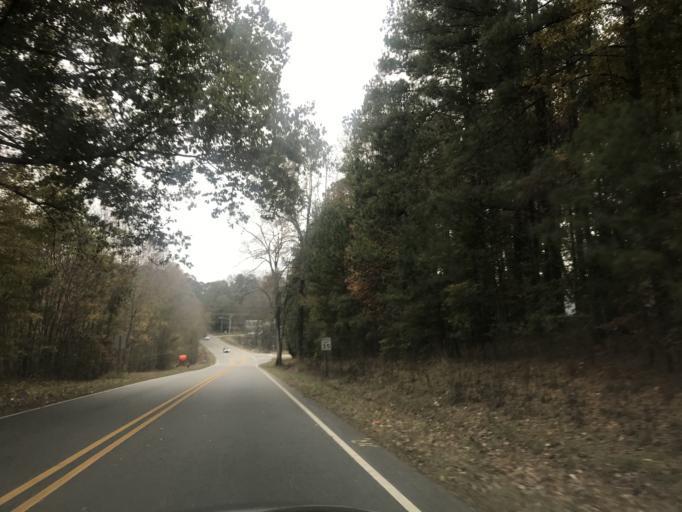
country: US
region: North Carolina
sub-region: Wake County
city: Wake Forest
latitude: 35.9944
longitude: -78.5015
